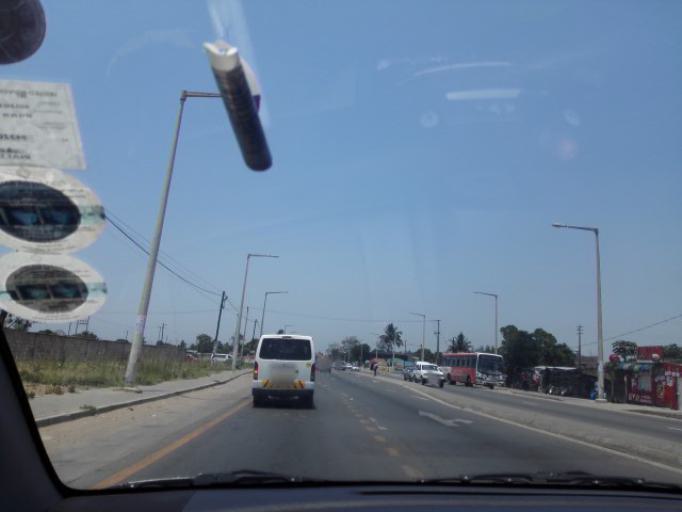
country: MZ
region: Maputo City
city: Maputo
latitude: -25.9210
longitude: 32.5631
